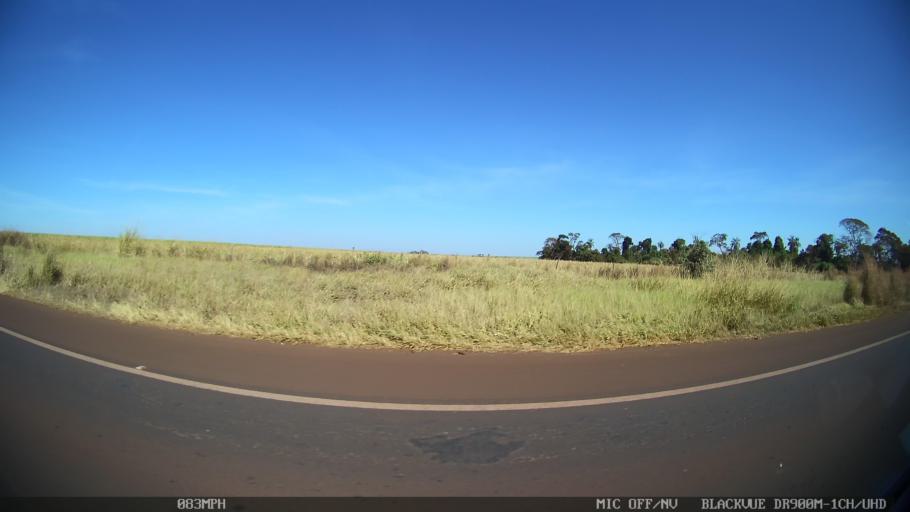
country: BR
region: Sao Paulo
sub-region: Guaira
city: Guaira
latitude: -20.4483
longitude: -48.1977
